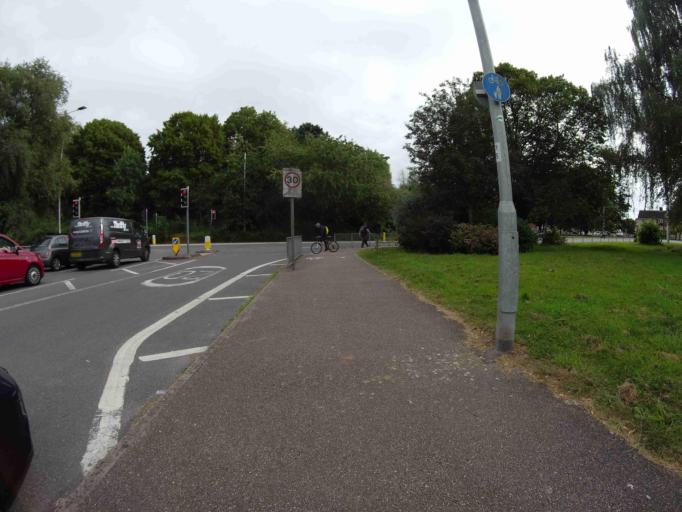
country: GB
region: England
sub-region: Devon
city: Heavitree
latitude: 50.7203
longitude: -3.4918
